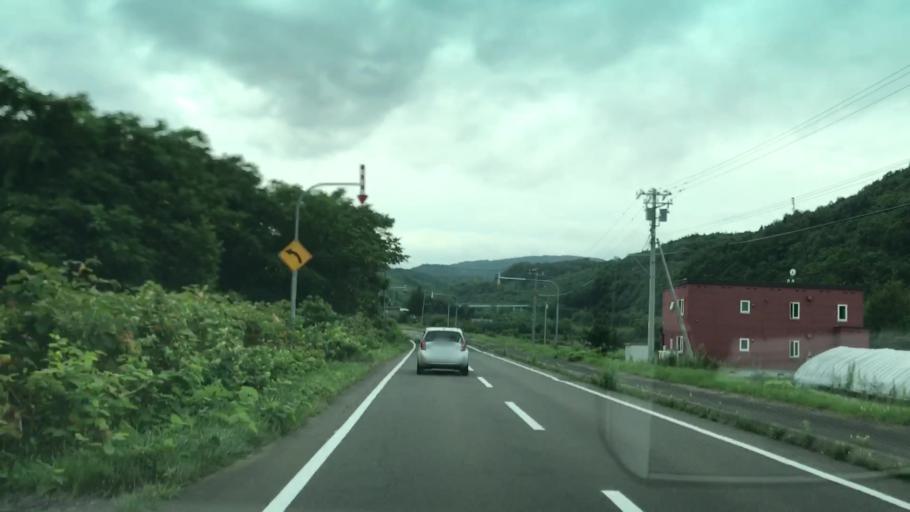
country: JP
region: Hokkaido
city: Yoichi
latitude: 43.1539
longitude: 140.8216
